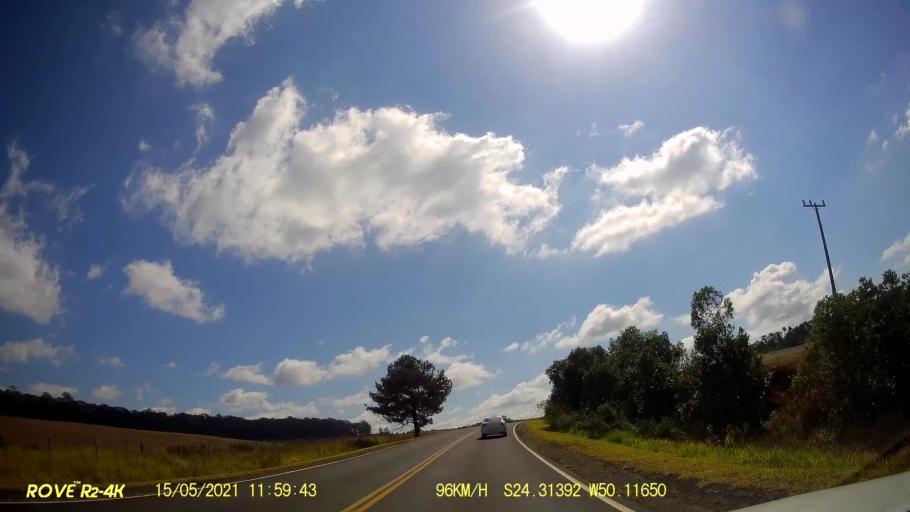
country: BR
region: Parana
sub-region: Pirai Do Sul
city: Pirai do Sul
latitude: -24.3141
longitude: -50.1164
